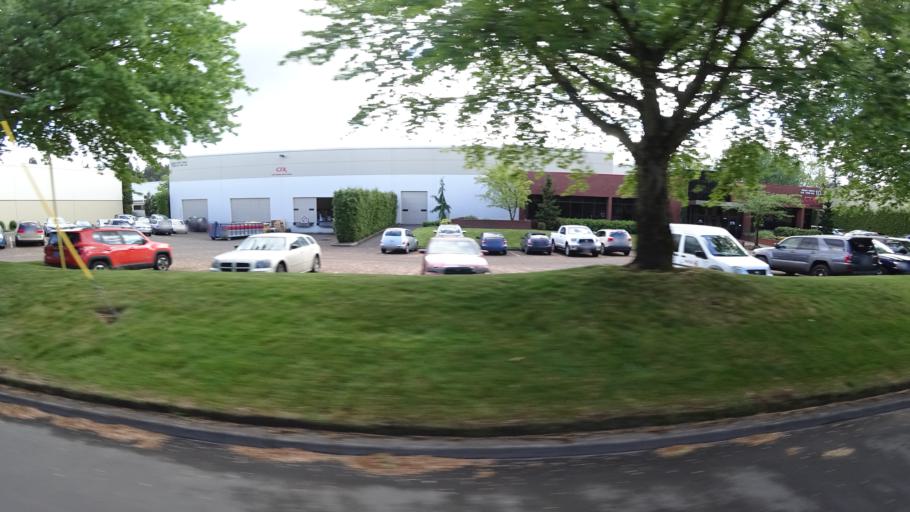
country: US
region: Oregon
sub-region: Washington County
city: Durham
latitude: 45.4007
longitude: -122.7491
